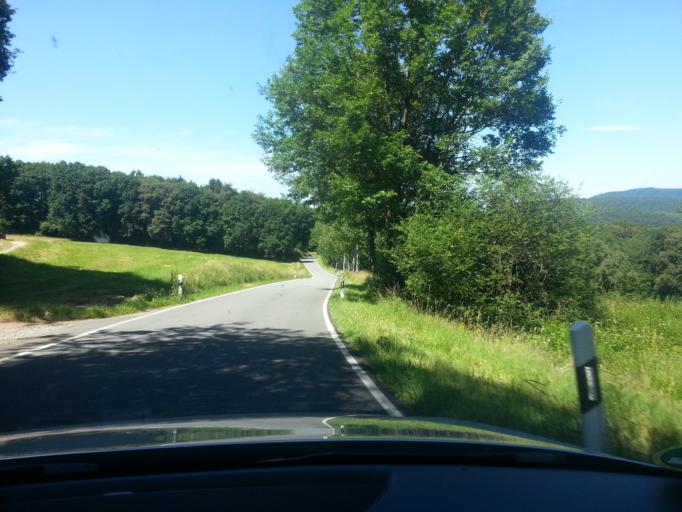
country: DE
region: Rheinland-Pfalz
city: Fockelberg
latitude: 49.5346
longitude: 7.4841
